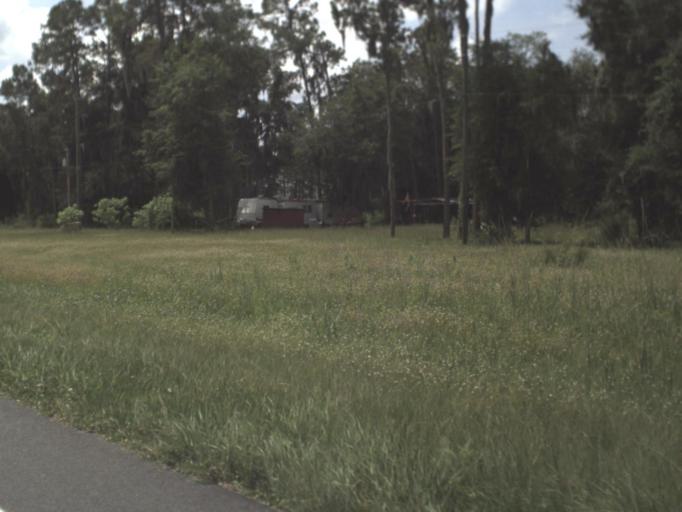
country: US
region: Florida
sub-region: Hamilton County
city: Jasper
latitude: 30.4786
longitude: -82.9151
